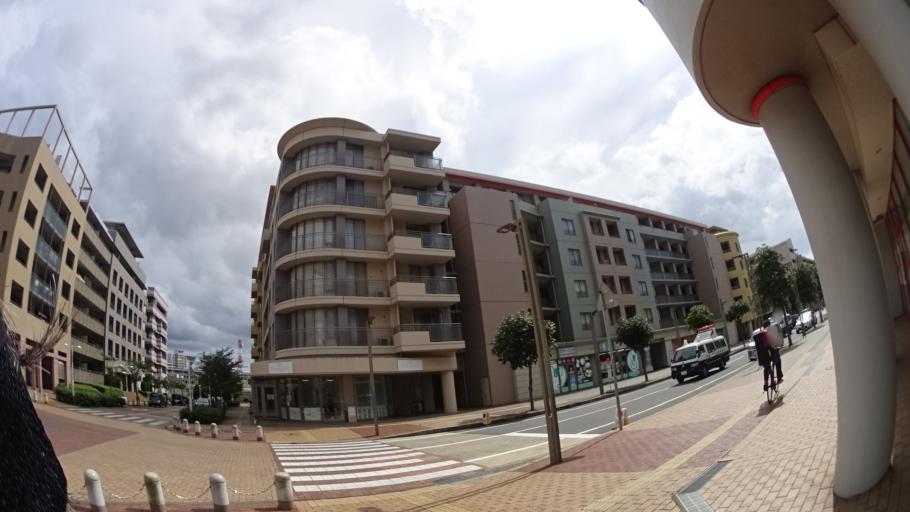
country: JP
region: Chiba
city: Funabashi
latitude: 35.6399
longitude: 140.0439
